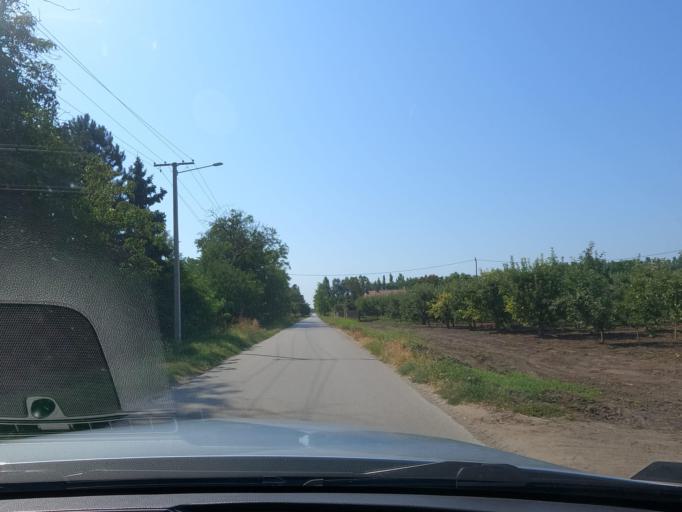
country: HU
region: Csongrad
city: Asotthalom
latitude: 46.0948
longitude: 19.7804
